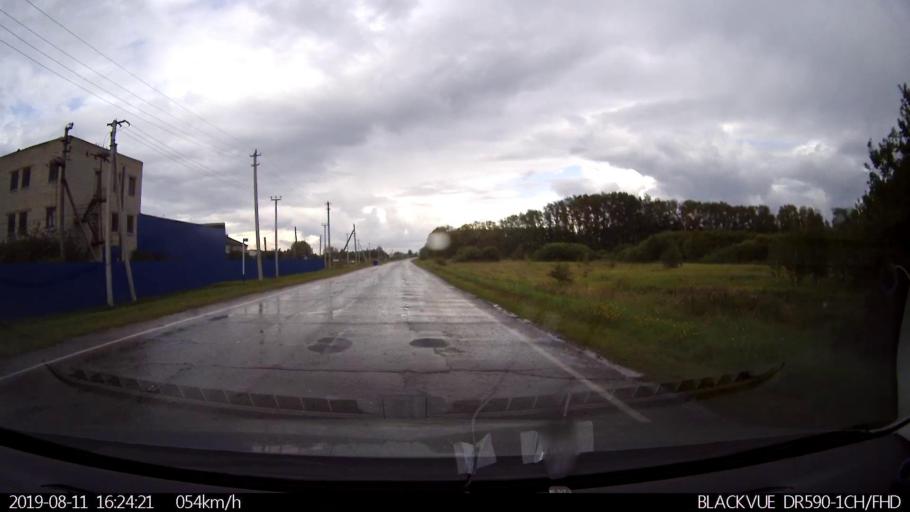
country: RU
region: Ulyanovsk
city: Mayna
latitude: 54.0999
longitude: 47.5936
